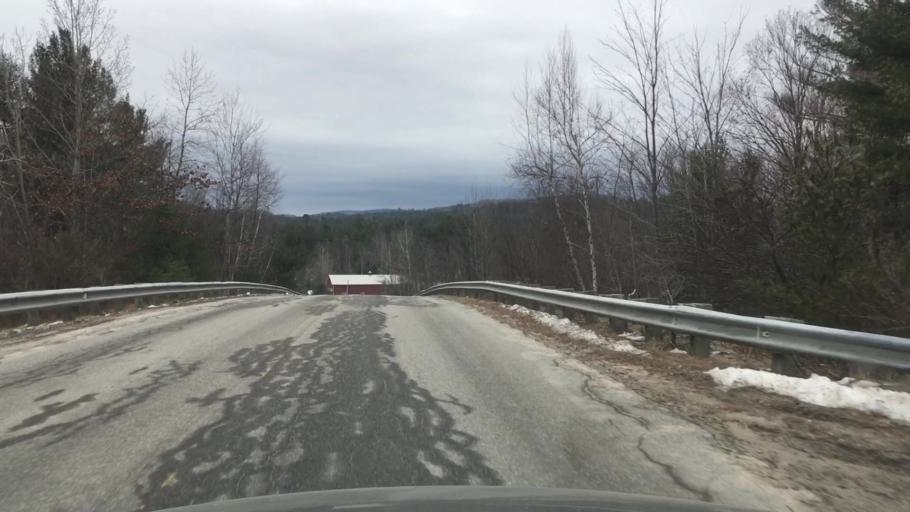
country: US
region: New Hampshire
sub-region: Hillsborough County
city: New Boston
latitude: 42.9966
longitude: -71.6605
